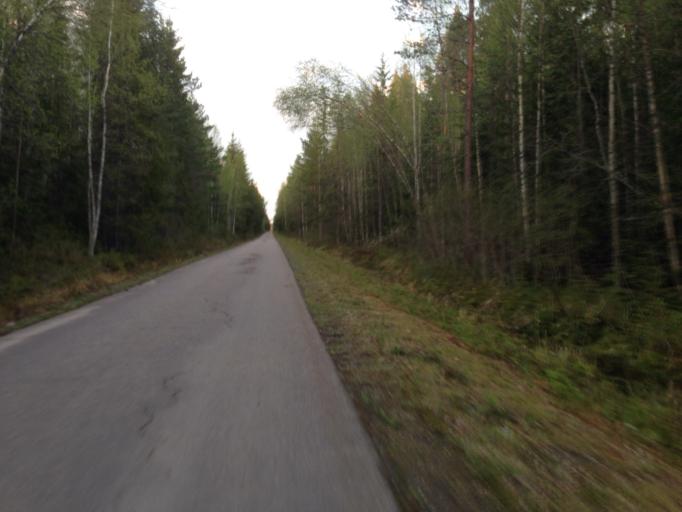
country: SE
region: Dalarna
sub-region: Ludvika Kommun
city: Ludvika
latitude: 60.1408
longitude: 15.1083
